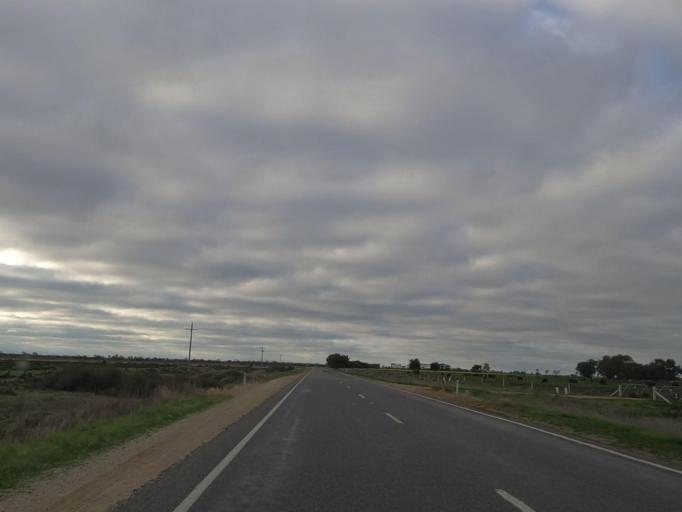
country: AU
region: Victoria
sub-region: Swan Hill
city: Swan Hill
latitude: -35.8345
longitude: 143.9425
